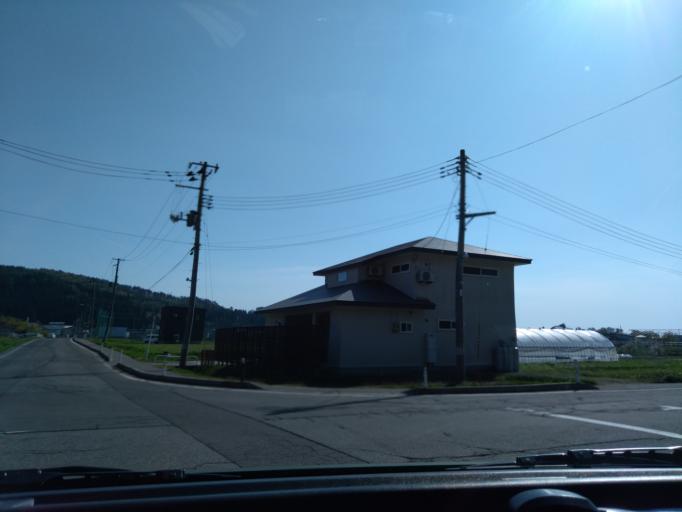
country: JP
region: Akita
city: Yokotemachi
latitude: 39.3089
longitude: 140.5847
